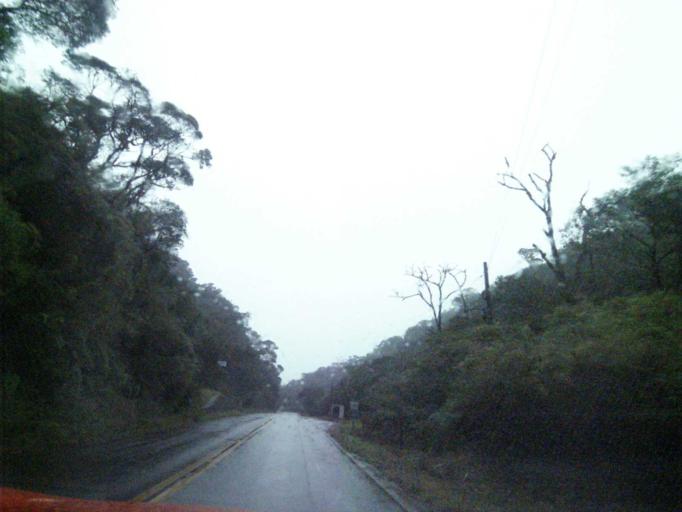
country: BR
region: Santa Catarina
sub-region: Anitapolis
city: Anitapolis
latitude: -27.7651
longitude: -49.0392
